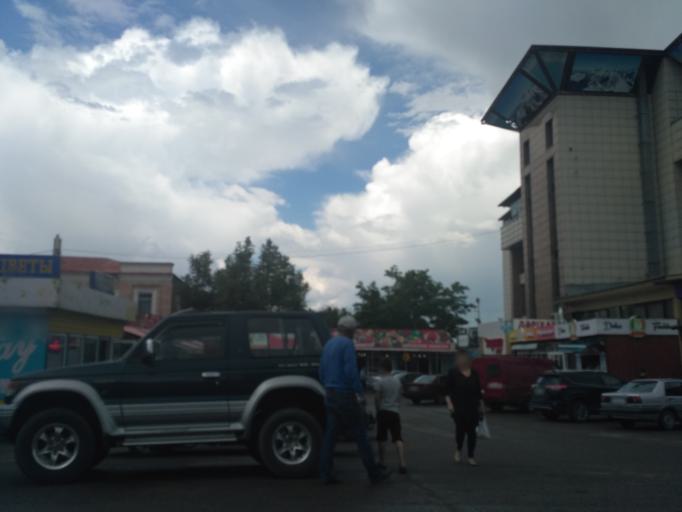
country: KZ
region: Almaty Oblysy
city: Burunday
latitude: 43.2032
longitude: 76.6193
